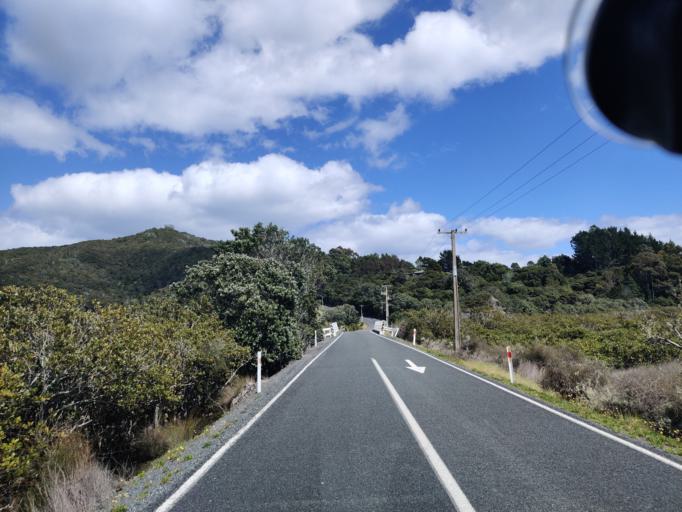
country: NZ
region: Northland
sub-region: Far North District
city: Paihia
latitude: -35.2617
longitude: 174.2515
